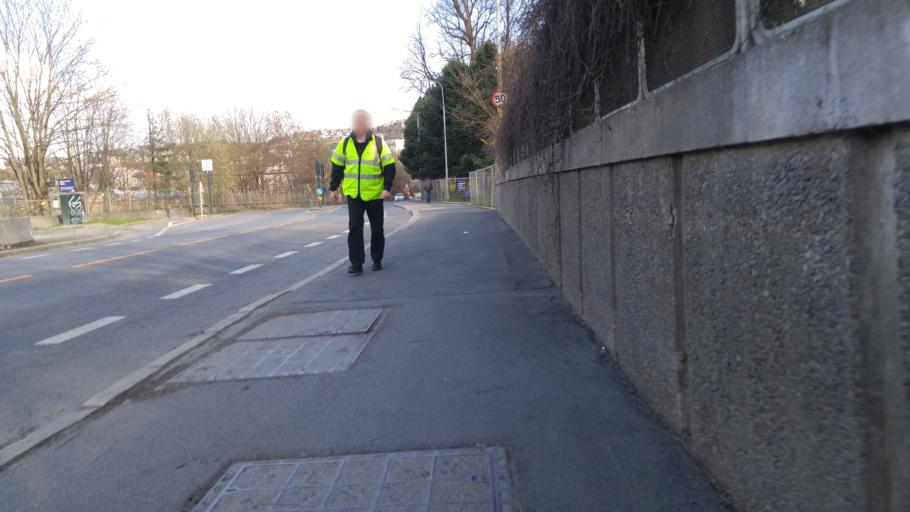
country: NO
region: Oslo
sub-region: Oslo
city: Oslo
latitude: 59.9049
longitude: 10.7704
